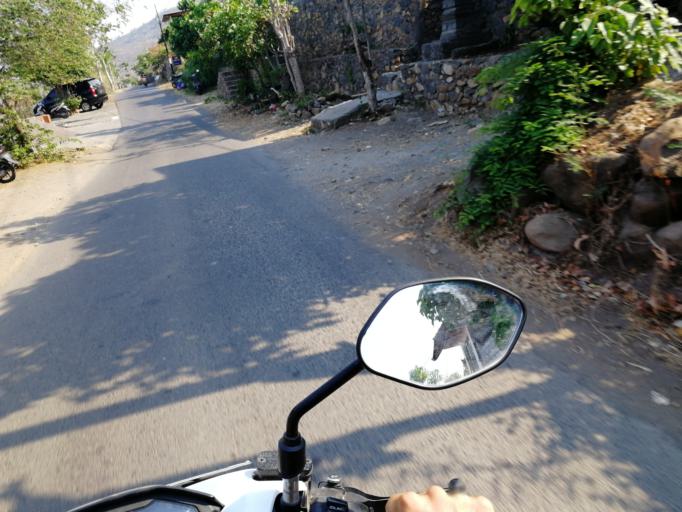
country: ID
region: Bali
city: Biaslantang Kaler
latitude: -8.3595
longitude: 115.6979
